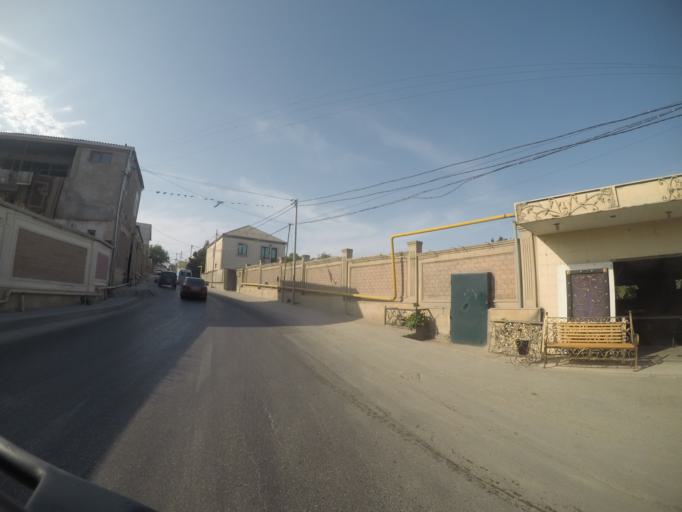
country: AZ
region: Baki
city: Binagadi
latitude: 40.4659
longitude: 49.8421
